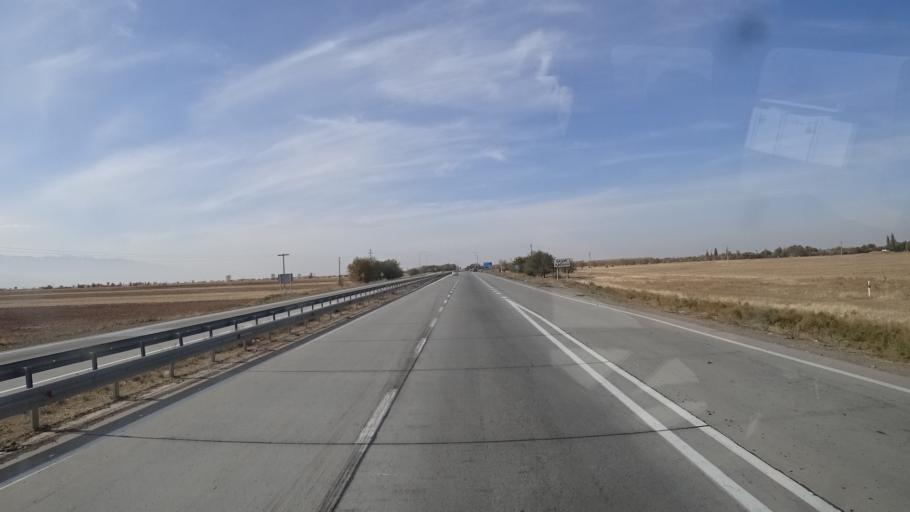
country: KZ
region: Zhambyl
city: Lugovoy
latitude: 42.9063
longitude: 72.9100
